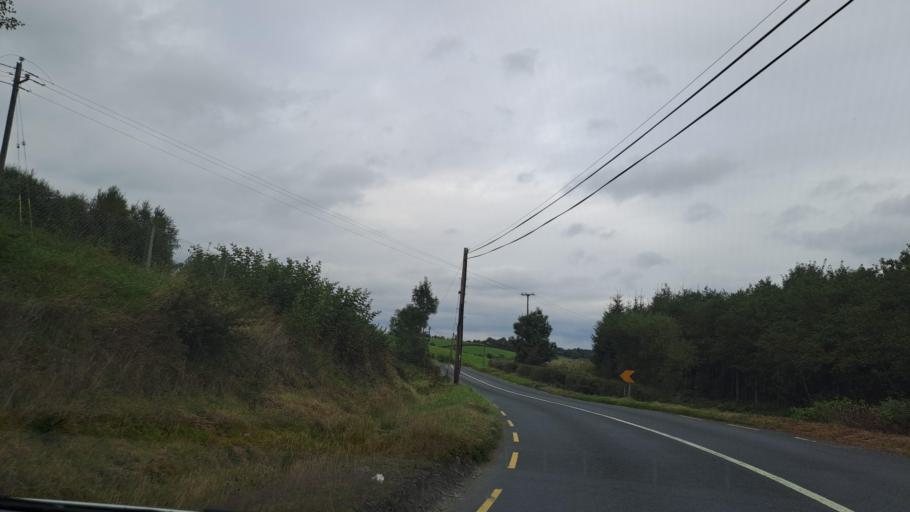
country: IE
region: Ulster
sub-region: An Cabhan
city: Bailieborough
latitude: 53.9318
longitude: -6.9650
